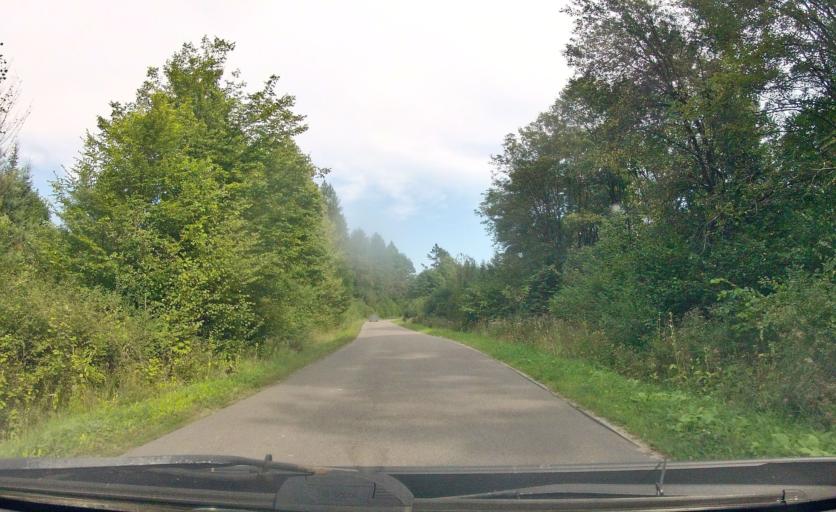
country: PL
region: Subcarpathian Voivodeship
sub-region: Powiat jasielski
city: Krempna
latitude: 49.4996
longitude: 21.5962
